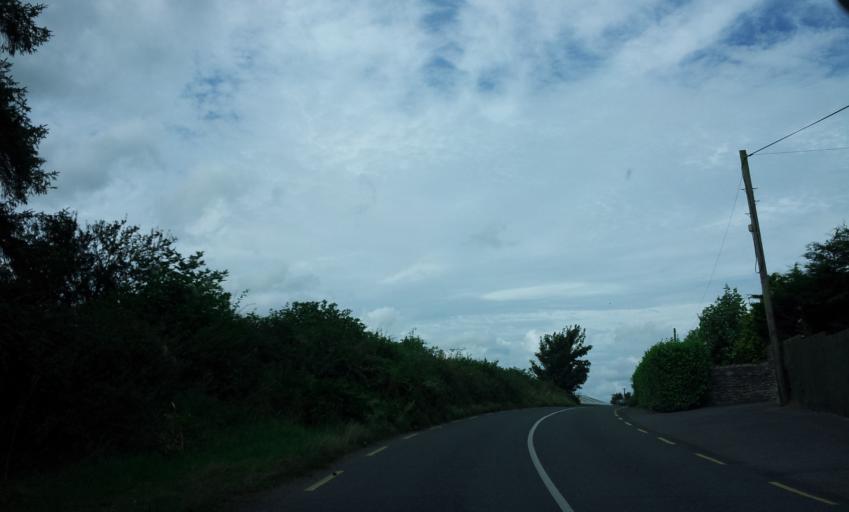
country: IE
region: Leinster
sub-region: Laois
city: Stradbally
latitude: 52.9685
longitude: -7.2091
